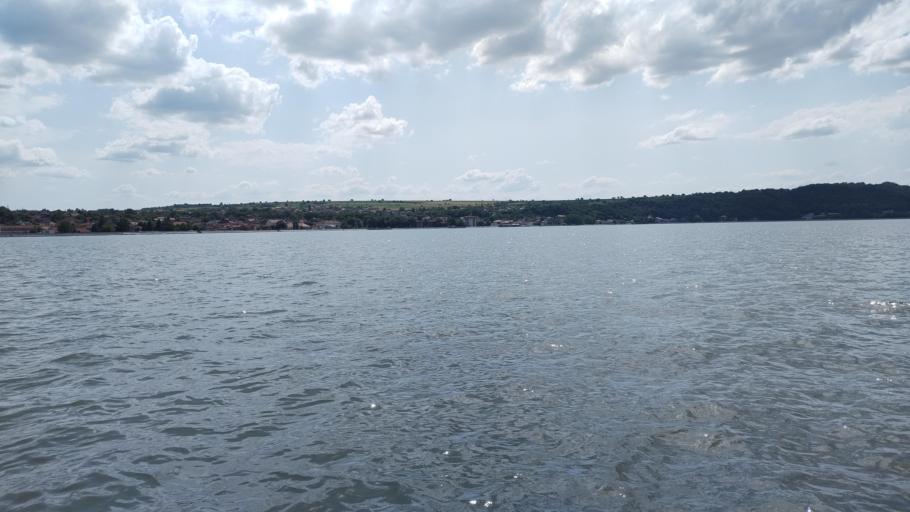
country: RS
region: Central Serbia
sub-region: Branicevski Okrug
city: Golubac
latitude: 44.6587
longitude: 21.6406
